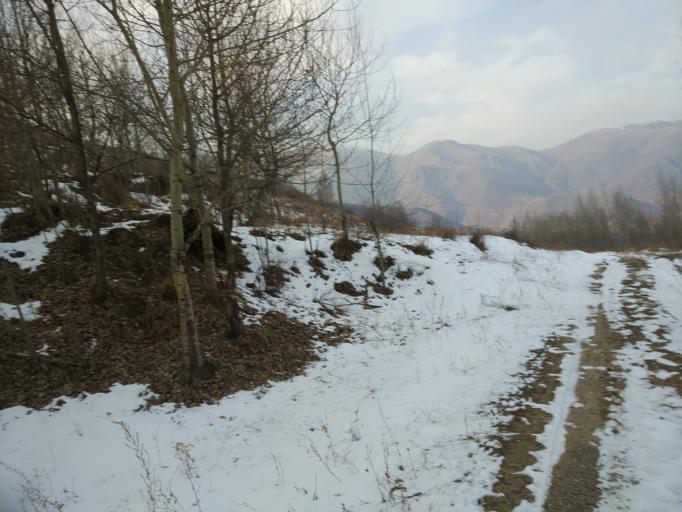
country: CN
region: Hebei
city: Xiwanzi
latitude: 40.7988
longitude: 115.4587
